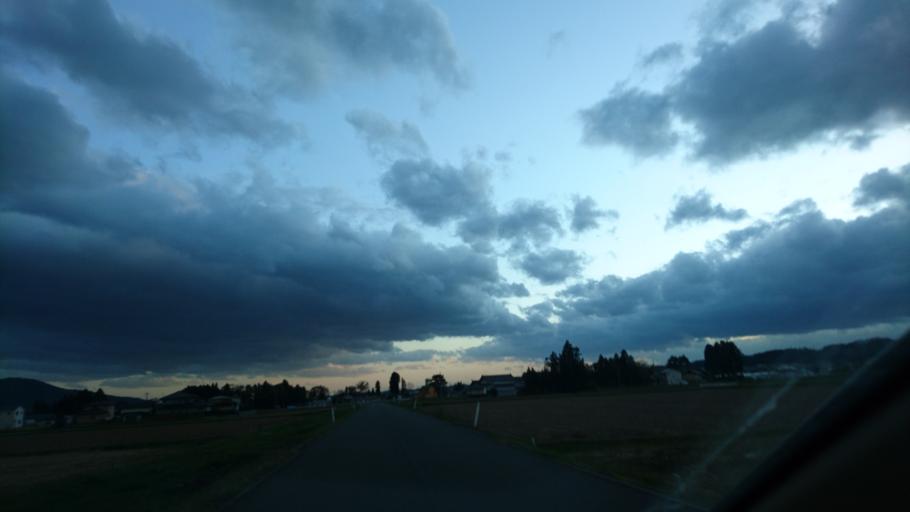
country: JP
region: Iwate
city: Mizusawa
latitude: 39.0673
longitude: 141.1413
